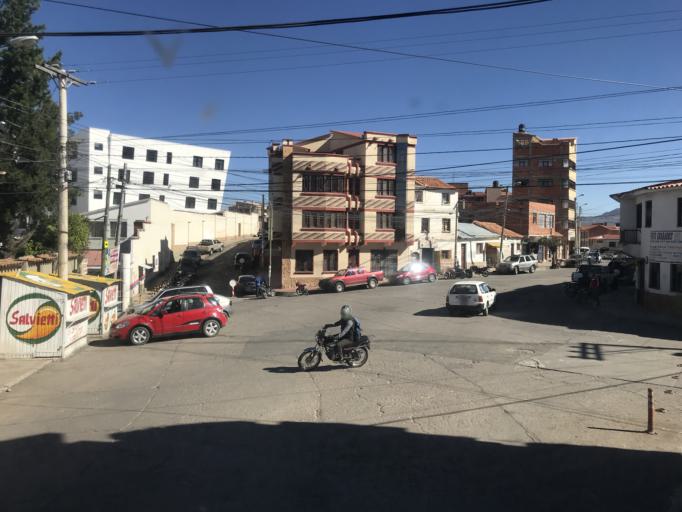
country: BO
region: Chuquisaca
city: Sucre
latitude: -19.0424
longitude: -65.2478
